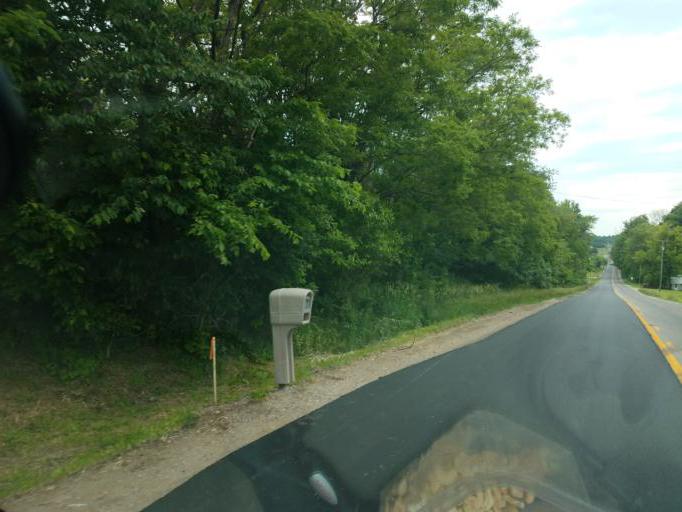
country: US
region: Ohio
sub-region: Richland County
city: Lexington
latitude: 40.5593
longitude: -82.6619
